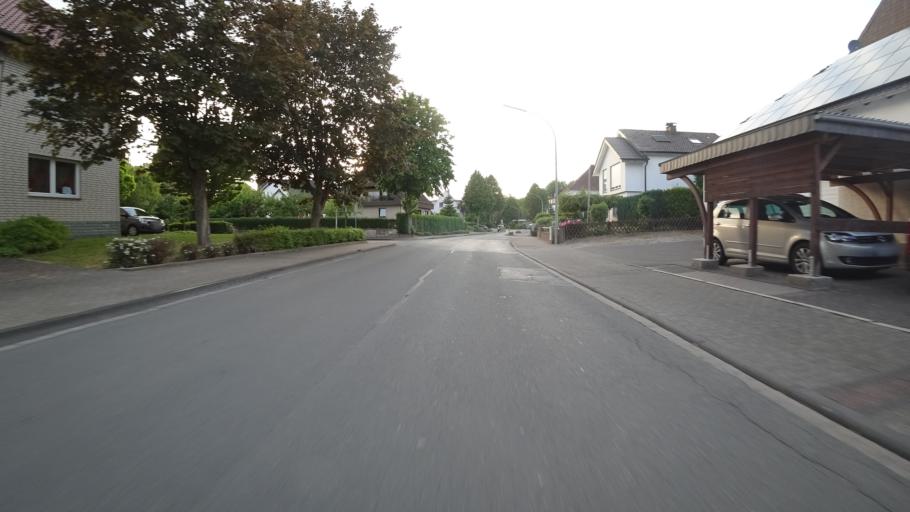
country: DE
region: North Rhine-Westphalia
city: Erwitte
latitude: 51.6350
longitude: 8.3594
